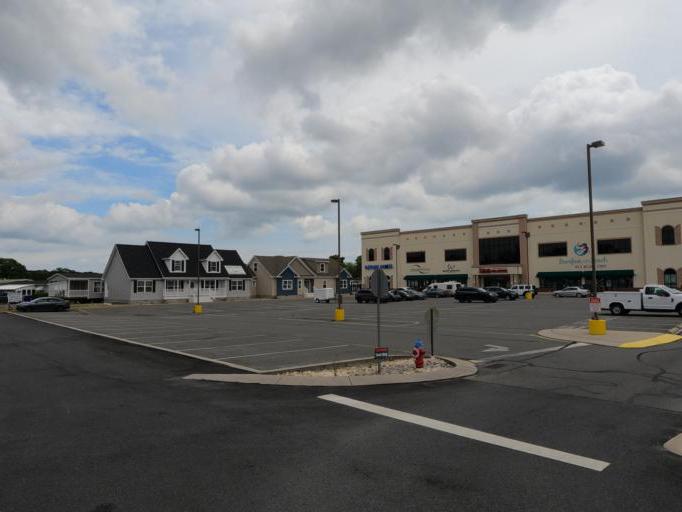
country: US
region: Delaware
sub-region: Sussex County
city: Lewes
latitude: 38.7351
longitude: -75.1367
